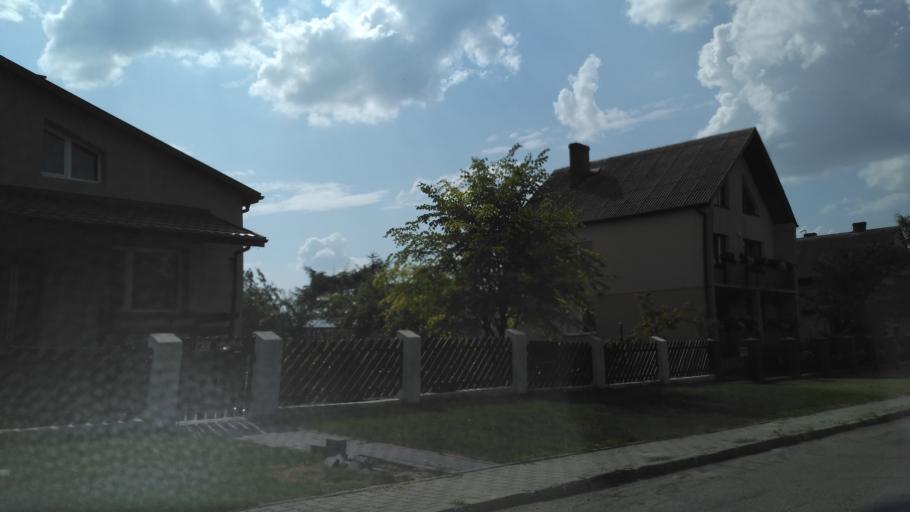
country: PL
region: Lublin Voivodeship
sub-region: Powiat chelmski
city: Rejowiec Fabryczny
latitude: 51.1860
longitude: 23.1679
